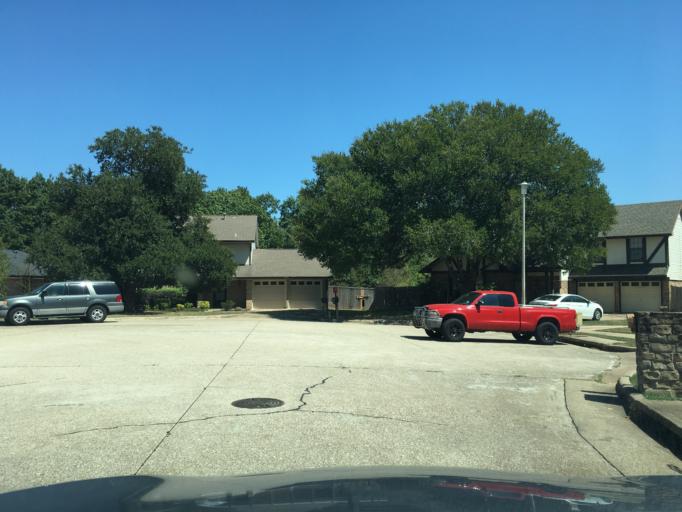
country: US
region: Texas
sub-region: Dallas County
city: Garland
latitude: 32.9510
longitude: -96.6340
